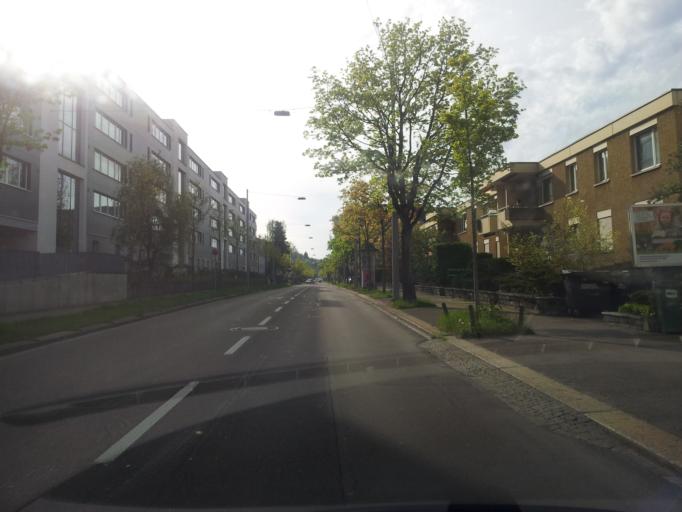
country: CH
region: Zurich
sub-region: Bezirk Zuerich
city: Zuerich (Kreis 11) / Oerlikon
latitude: 47.4099
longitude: 8.5356
